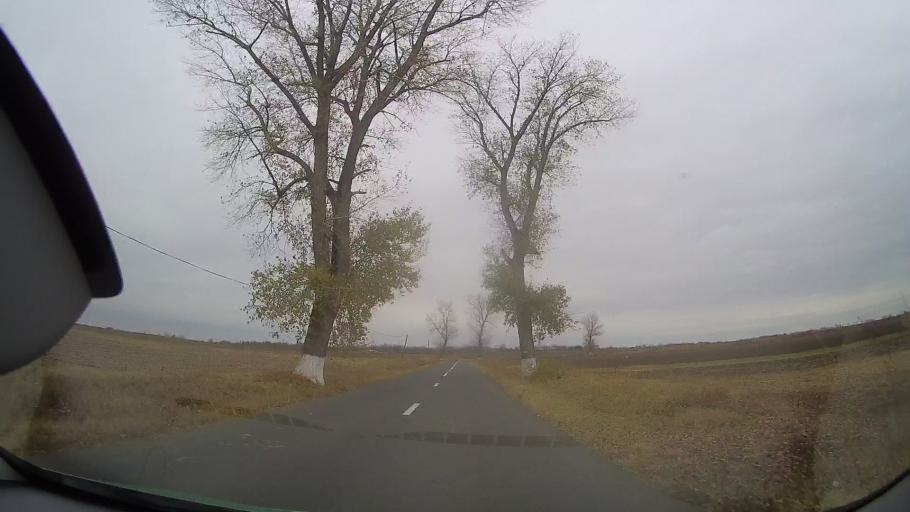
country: RO
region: Braila
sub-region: Comuna Budesti
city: Tataru
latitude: 44.8391
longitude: 27.4194
